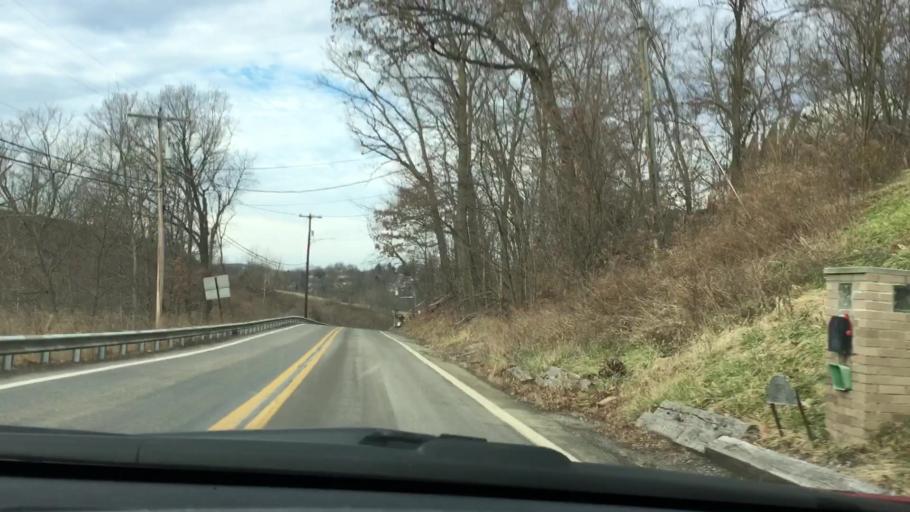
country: US
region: Pennsylvania
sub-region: Allegheny County
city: Jefferson Hills
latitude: 40.2756
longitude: -79.9485
